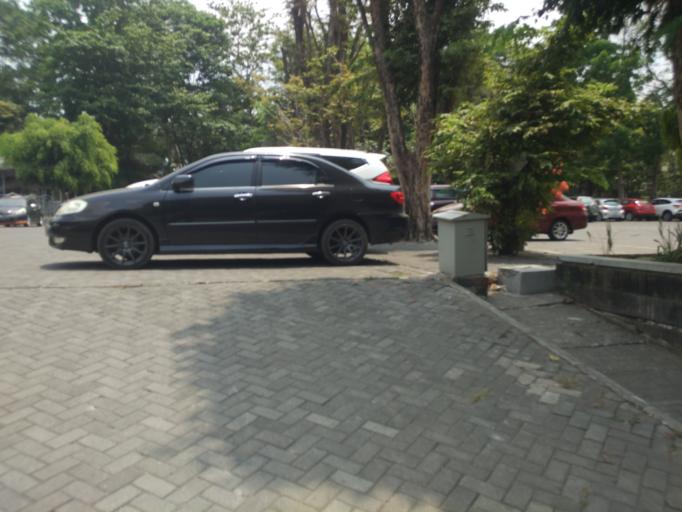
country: ID
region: Daerah Istimewa Yogyakarta
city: Sleman
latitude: -7.6872
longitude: 110.4149
